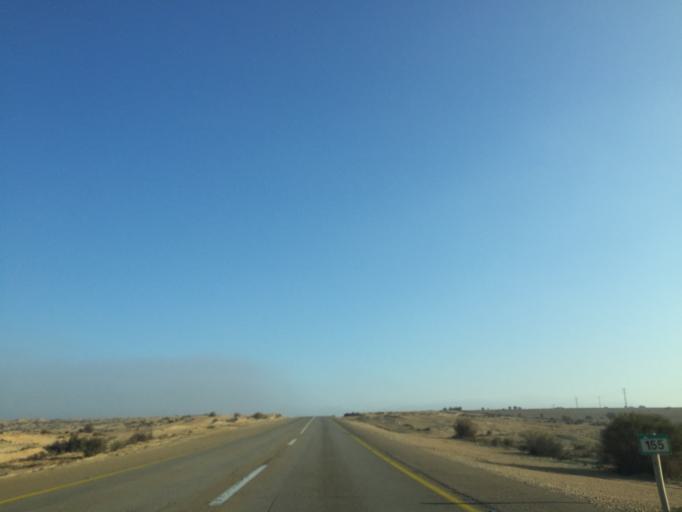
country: IL
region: Southern District
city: Yeroham
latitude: 31.0026
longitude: 34.9468
